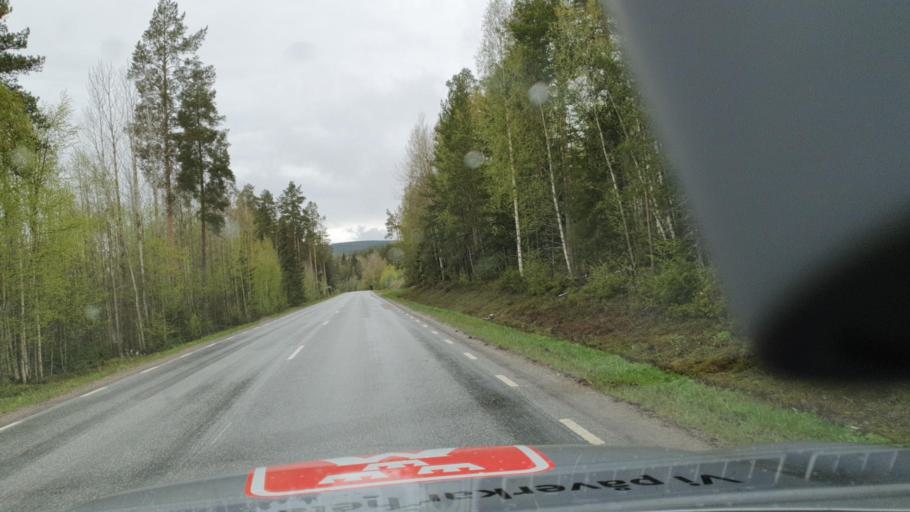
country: SE
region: Vaesternorrland
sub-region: OErnskoeldsviks Kommun
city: Bjasta
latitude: 63.3408
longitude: 18.5361
